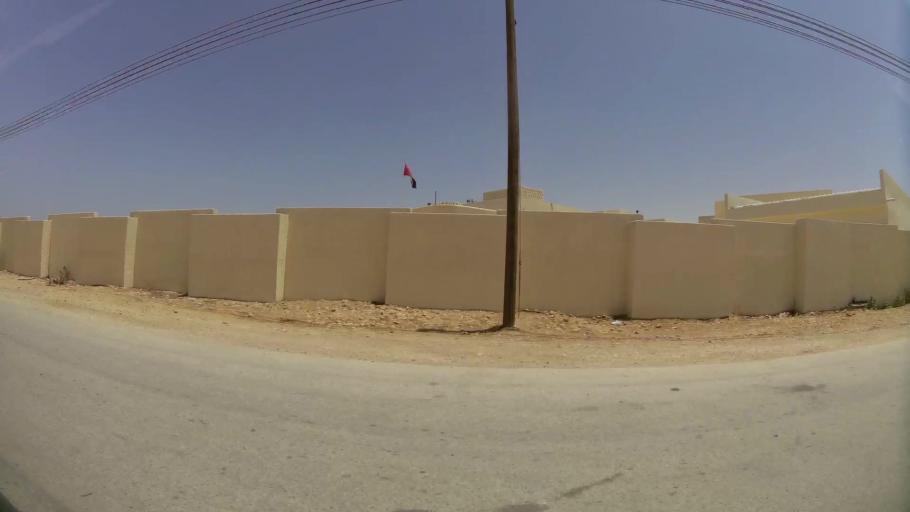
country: OM
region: Zufar
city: Salalah
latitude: 17.0727
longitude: 54.1499
